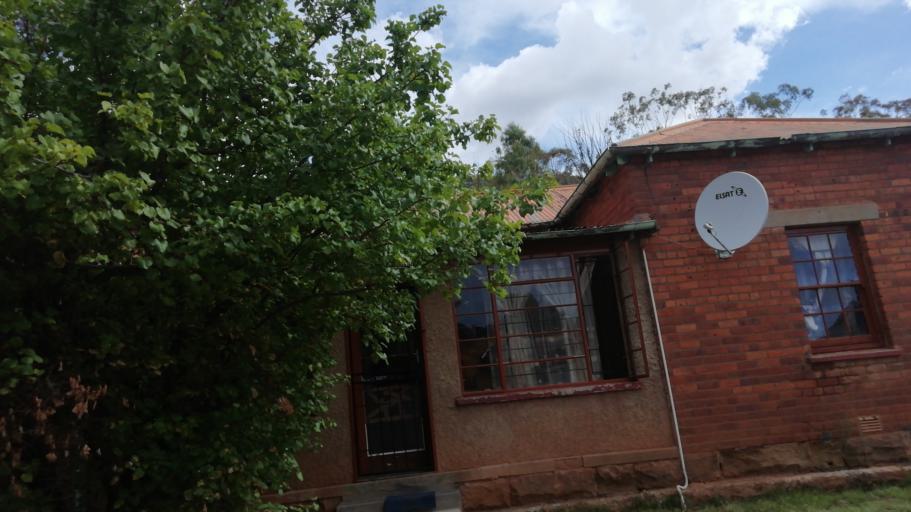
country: LS
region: Maseru
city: Nako
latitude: -29.6317
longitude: 27.5013
